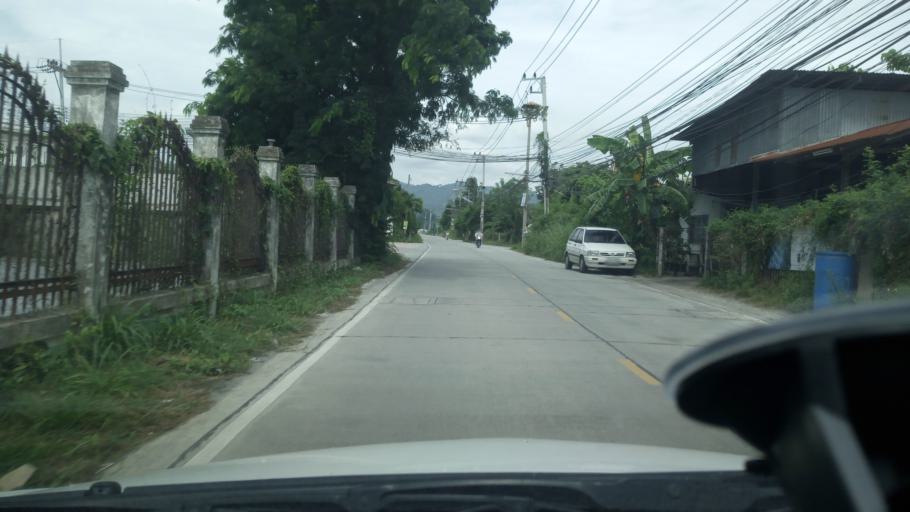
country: TH
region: Chon Buri
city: Chon Buri
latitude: 13.2942
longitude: 100.9636
